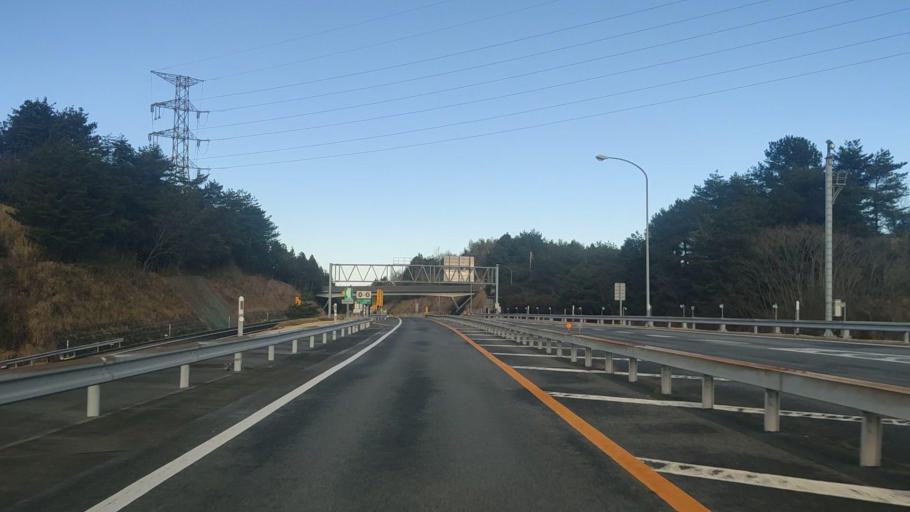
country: JP
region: Oita
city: Hiji
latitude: 33.3781
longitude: 131.4521
